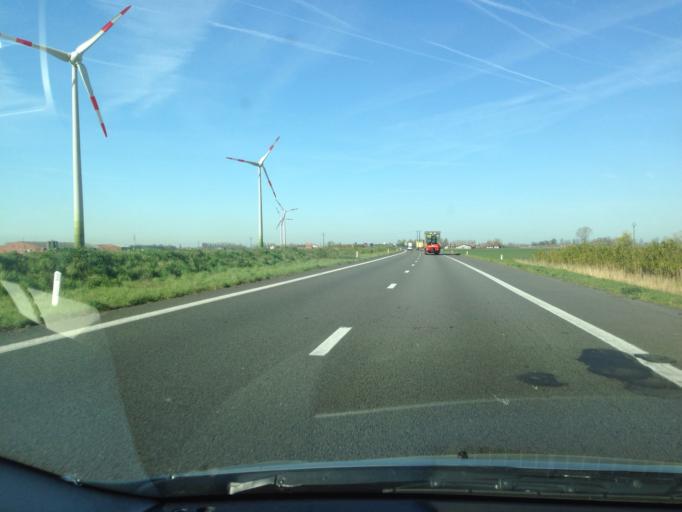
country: BE
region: Flanders
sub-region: Provincie West-Vlaanderen
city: Gistel
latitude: 51.1683
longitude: 2.9653
